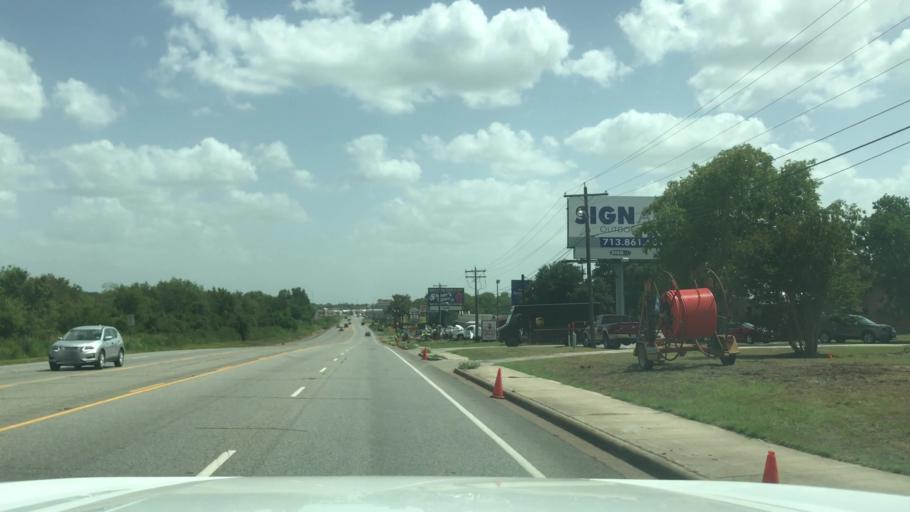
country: US
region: Texas
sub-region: Robertson County
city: Hearne
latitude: 30.8928
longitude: -96.6003
